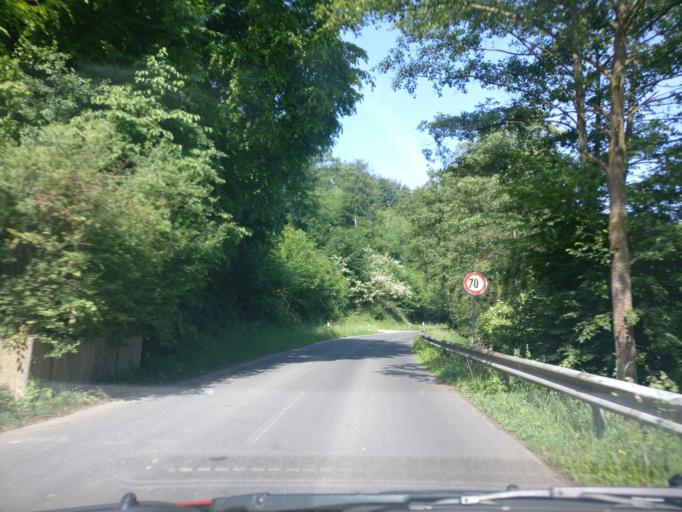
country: DE
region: Lower Saxony
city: Scheden
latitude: 51.3924
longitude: 9.7279
